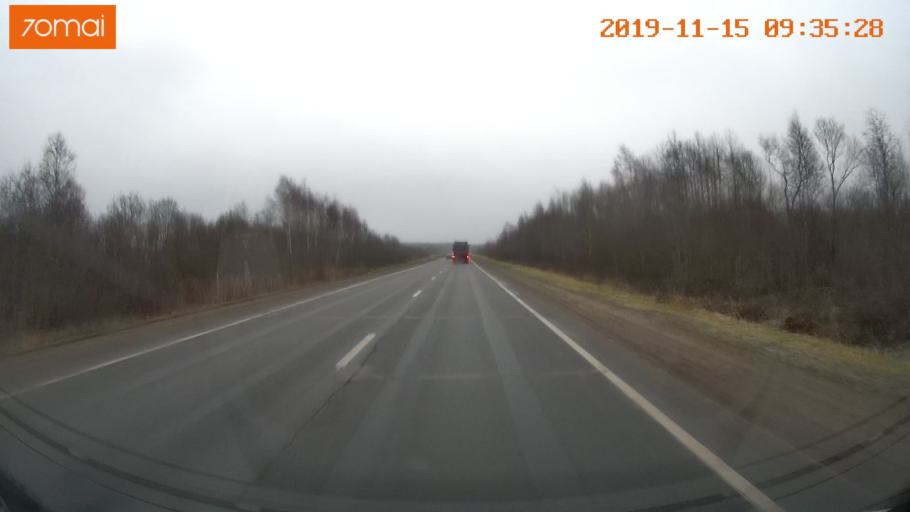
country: RU
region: Vologda
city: Sheksna
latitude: 59.2542
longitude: 38.3997
